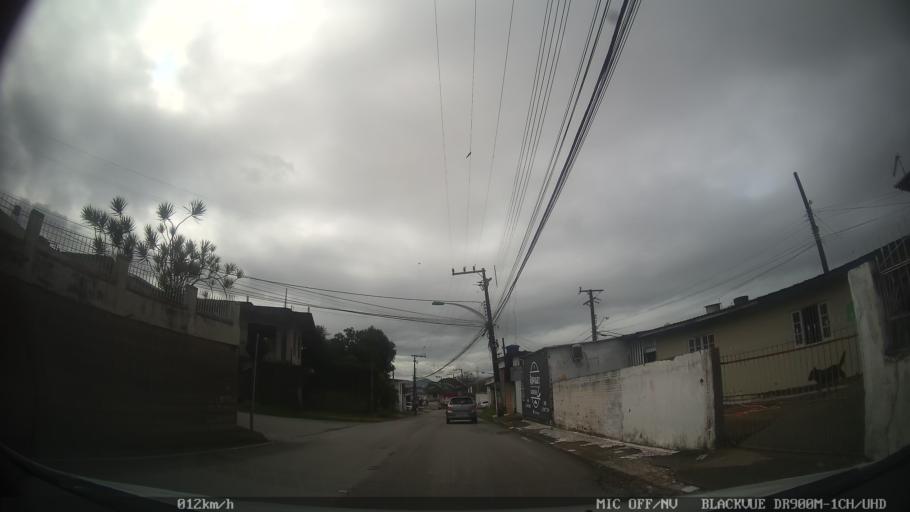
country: BR
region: Santa Catarina
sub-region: Biguacu
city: Biguacu
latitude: -27.5339
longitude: -48.6429
